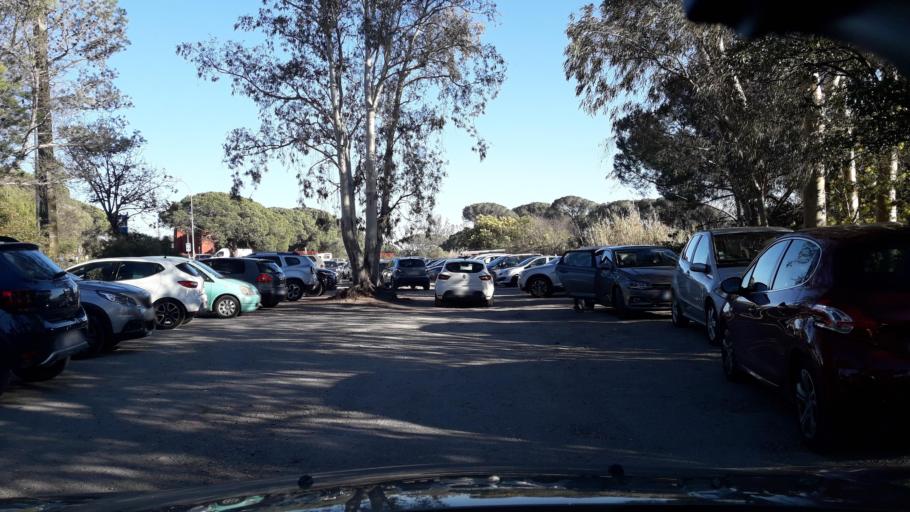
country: FR
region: Provence-Alpes-Cote d'Azur
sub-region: Departement du Var
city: Frejus
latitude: 43.4580
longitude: 6.7254
